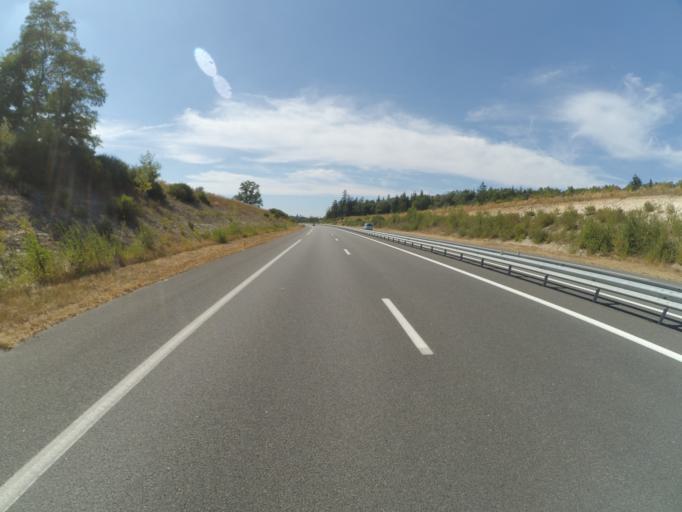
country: FR
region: Limousin
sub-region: Departement de la Haute-Vienne
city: Veyrac
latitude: 45.8864
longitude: 1.0760
